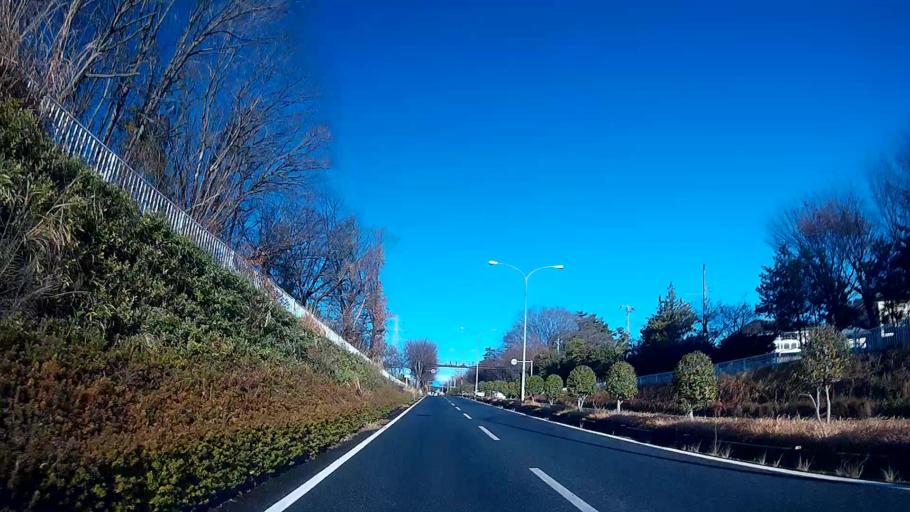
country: JP
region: Saitama
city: Hanno
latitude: 35.8542
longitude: 139.3592
